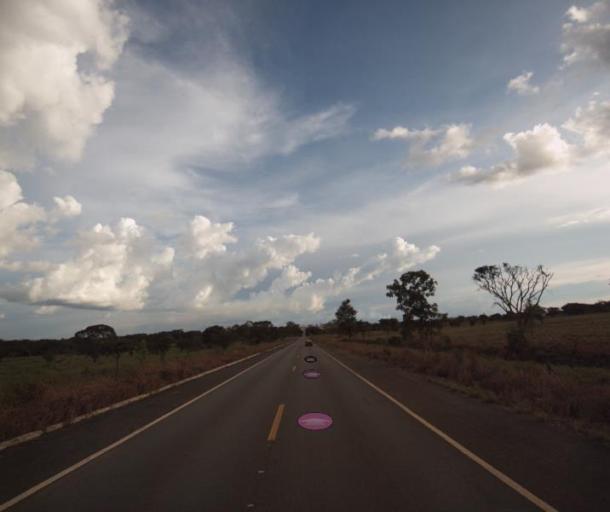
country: BR
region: Goias
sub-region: Niquelandia
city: Niquelandia
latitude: -14.7270
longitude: -48.6110
